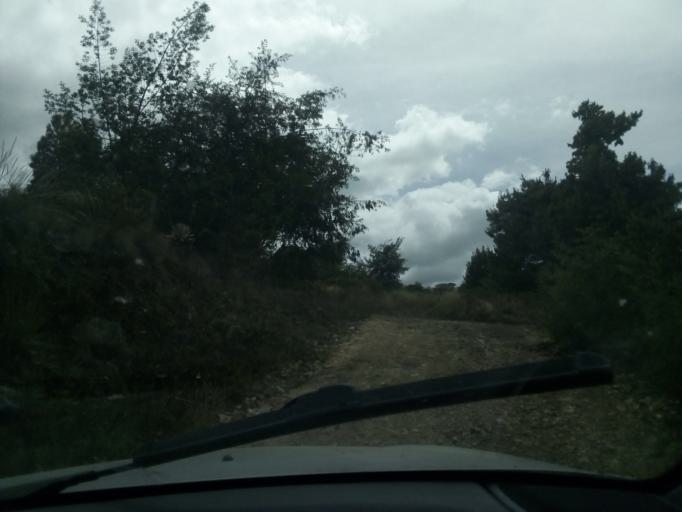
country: CO
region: Boyaca
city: Toca
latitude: 5.6057
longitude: -73.1119
